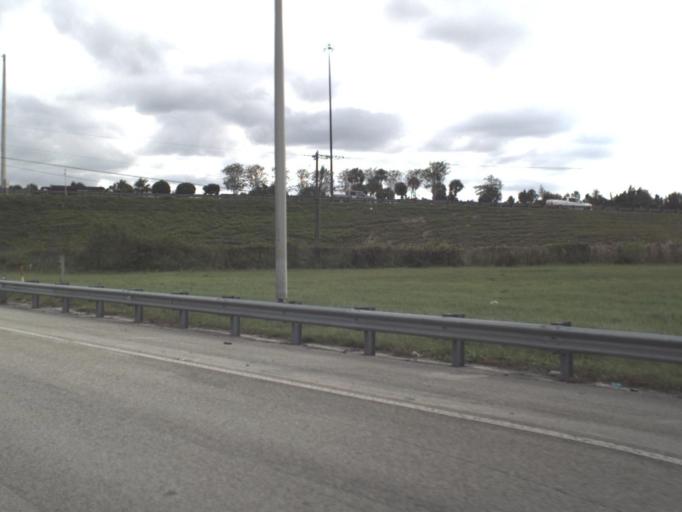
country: US
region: Florida
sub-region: Palm Beach County
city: Limestone Creek
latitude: 26.9360
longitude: -80.1545
